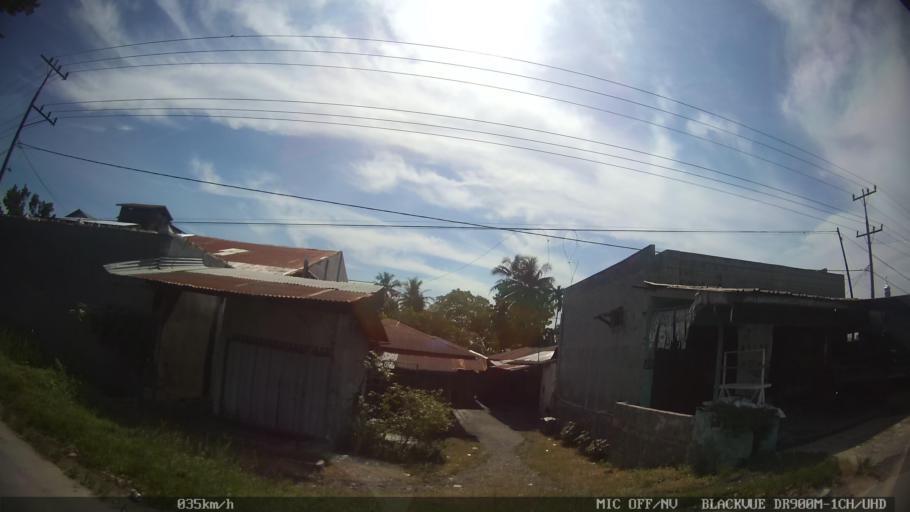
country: ID
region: North Sumatra
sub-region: Kabupaten Langkat
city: Stabat
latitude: 3.6789
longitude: 98.5092
